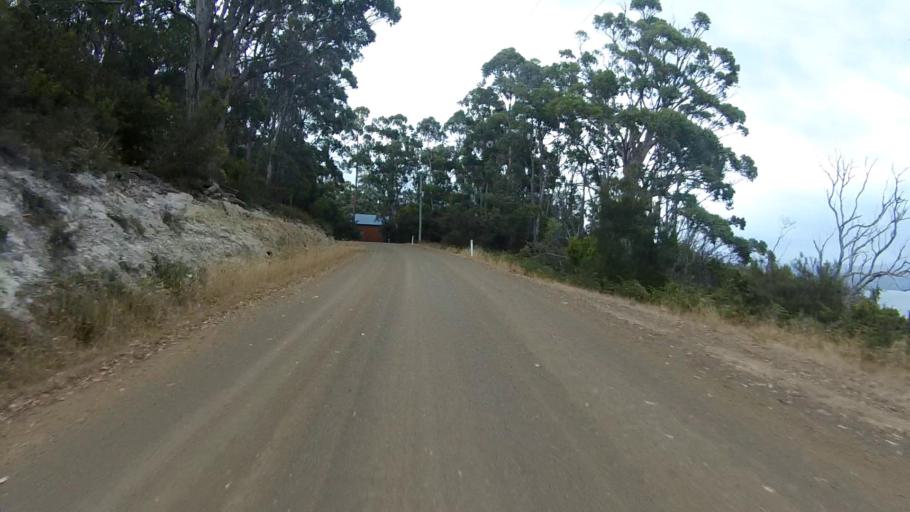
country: AU
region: Tasmania
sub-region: Huon Valley
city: Cygnet
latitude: -43.2396
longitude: 147.0979
